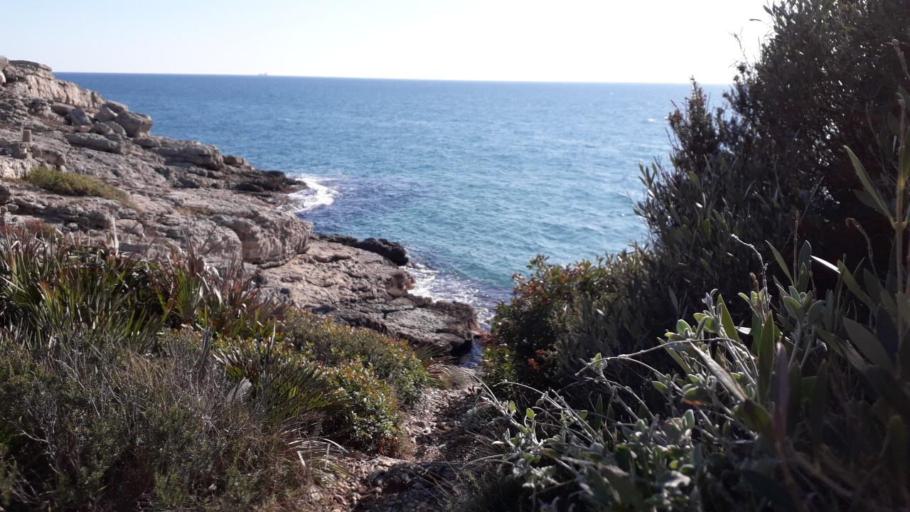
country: ES
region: Catalonia
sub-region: Provincia de Tarragona
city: Salou
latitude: 41.0563
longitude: 1.1626
